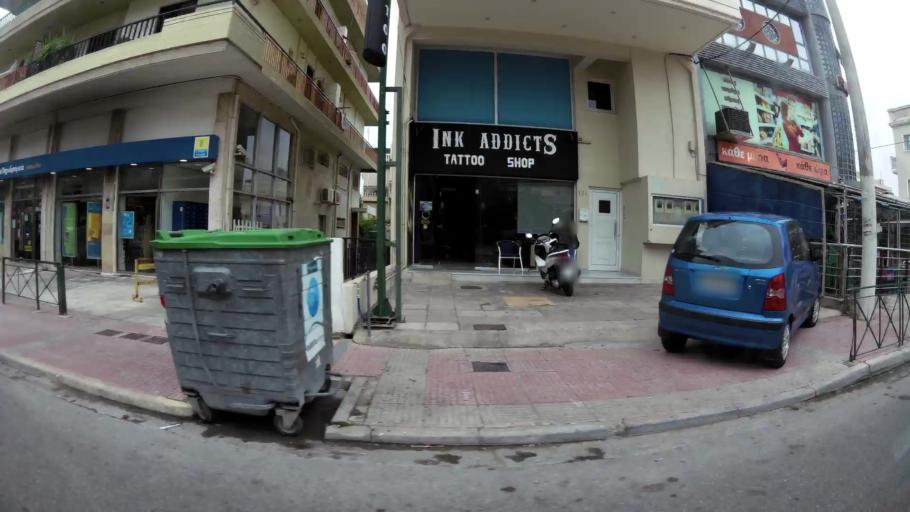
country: GR
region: Attica
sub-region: Nomarchia Athinas
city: Ilion
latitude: 38.0345
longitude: 23.7061
